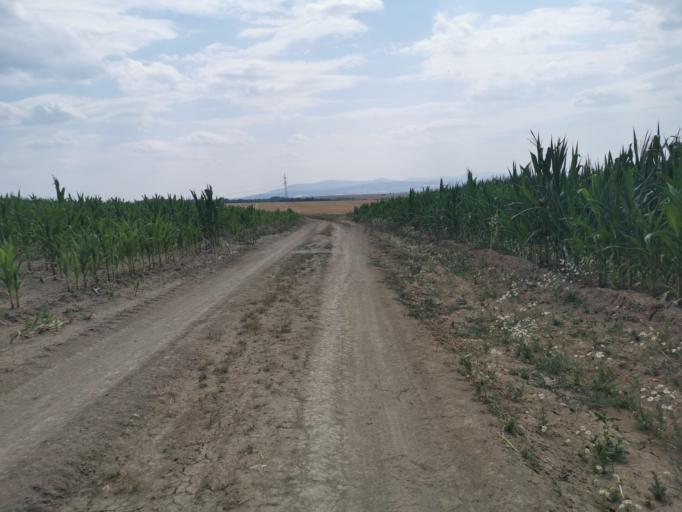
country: SK
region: Trnavsky
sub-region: Okres Senica
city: Senica
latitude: 48.6901
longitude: 17.4206
